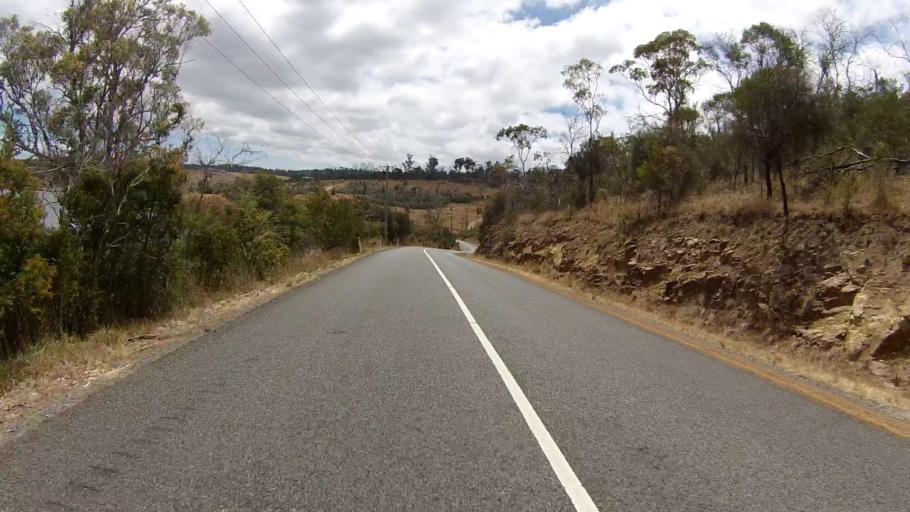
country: AU
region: Tasmania
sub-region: Sorell
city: Sorell
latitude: -42.8654
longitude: 147.6920
